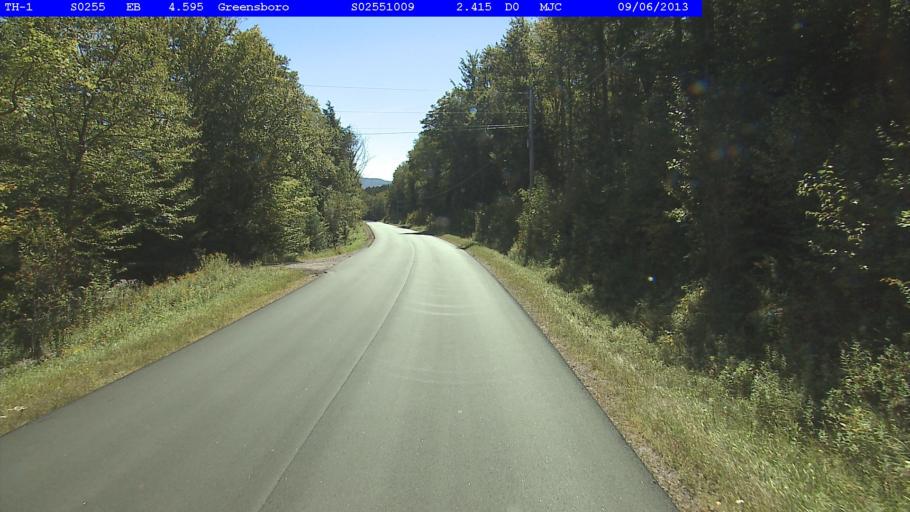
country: US
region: Vermont
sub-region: Caledonia County
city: Hardwick
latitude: 44.6085
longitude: -72.3183
